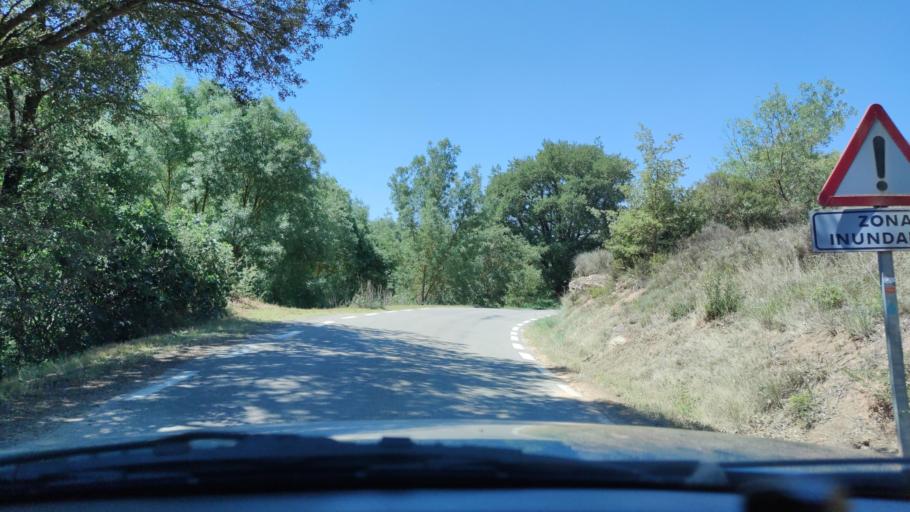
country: ES
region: Catalonia
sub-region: Provincia de Lleida
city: Tora de Riubregos
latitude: 41.8225
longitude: 1.4193
